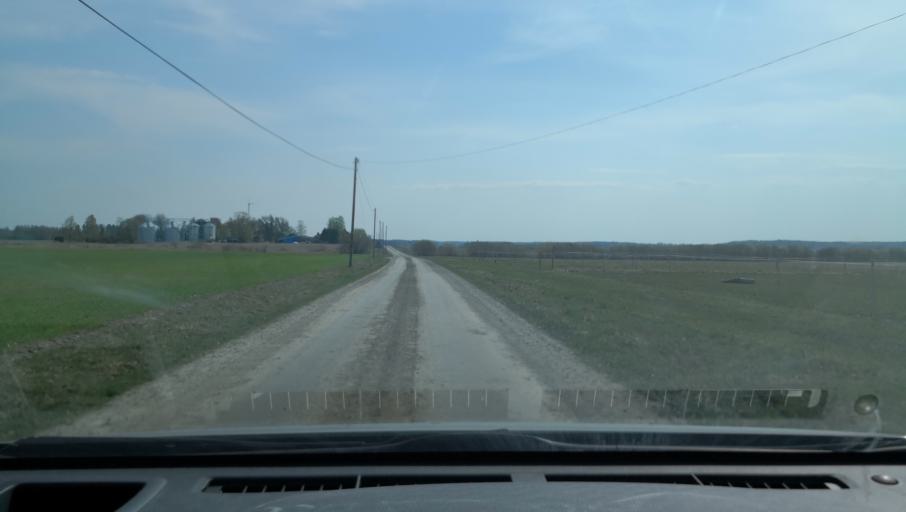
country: SE
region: Vaestmanland
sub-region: Vasteras
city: Skultuna
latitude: 59.7958
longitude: 16.4380
